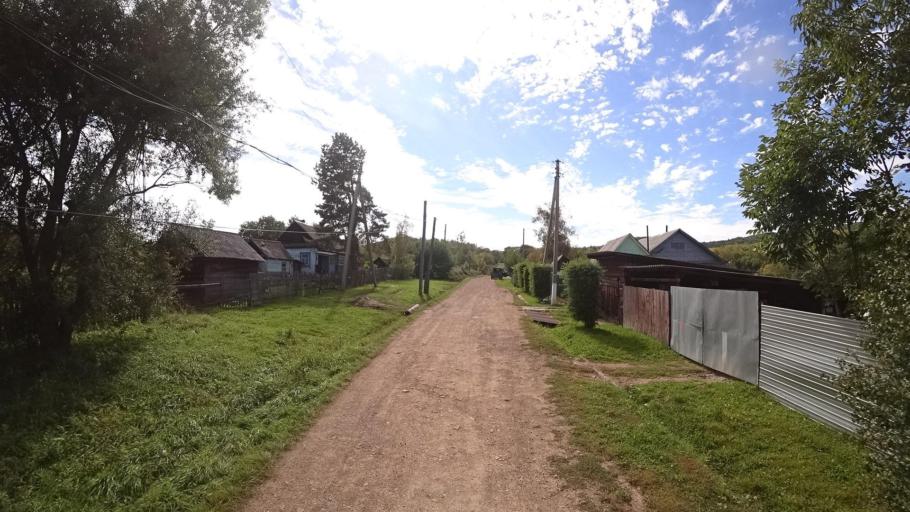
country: RU
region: Primorskiy
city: Yakovlevka
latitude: 44.3941
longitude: 133.6042
